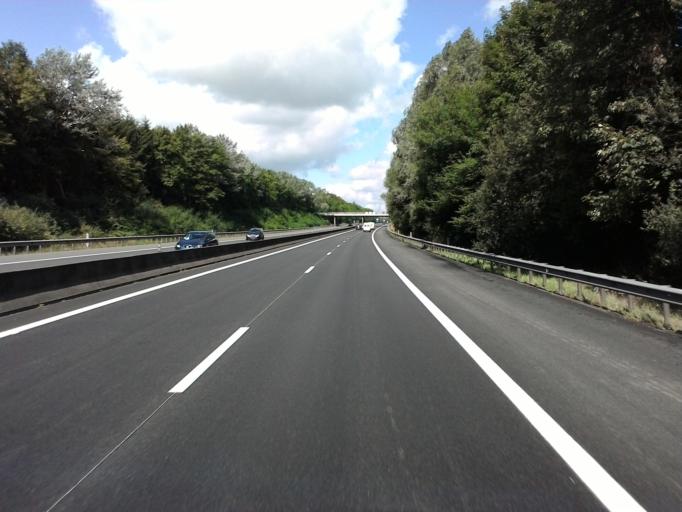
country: LU
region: Luxembourg
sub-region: Canton de Capellen
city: Mamer
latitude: 49.6329
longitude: 6.0349
